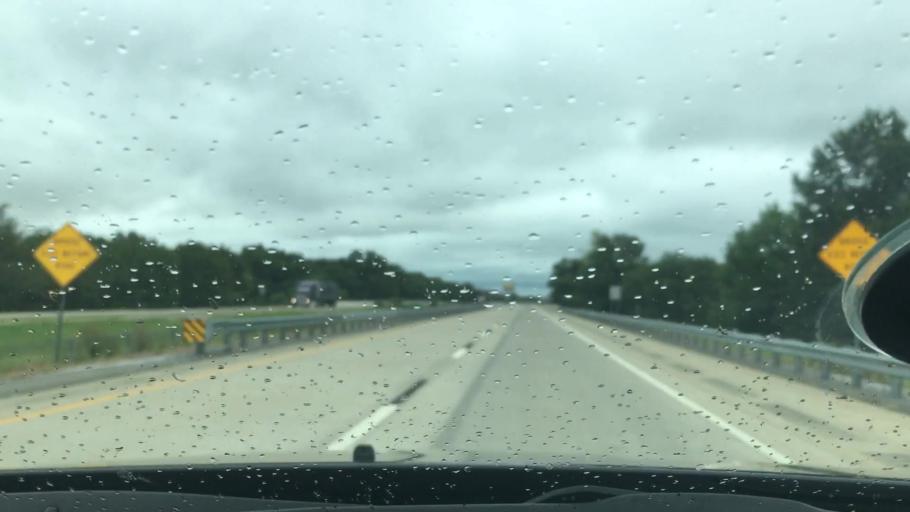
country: US
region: Oklahoma
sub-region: Muskogee County
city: Warner
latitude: 35.4860
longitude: -95.1912
